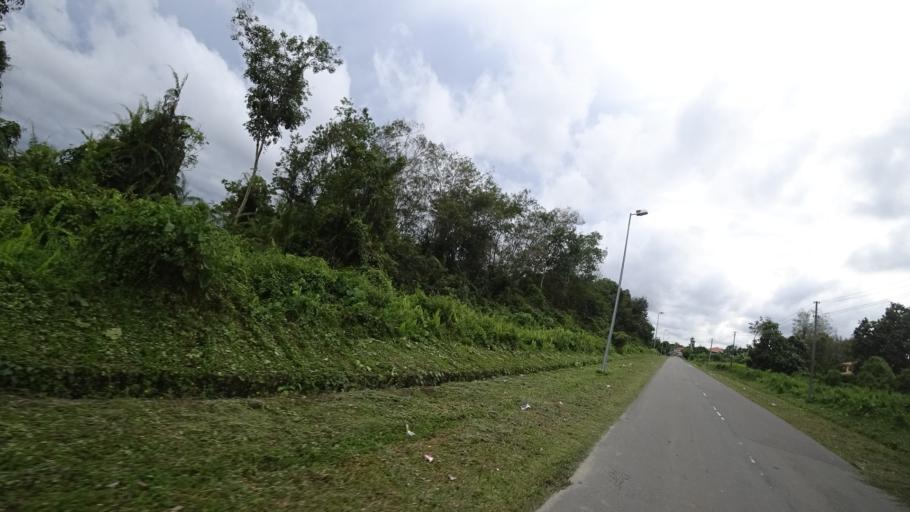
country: BN
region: Brunei and Muara
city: Bandar Seri Begawan
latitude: 4.8548
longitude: 114.8500
